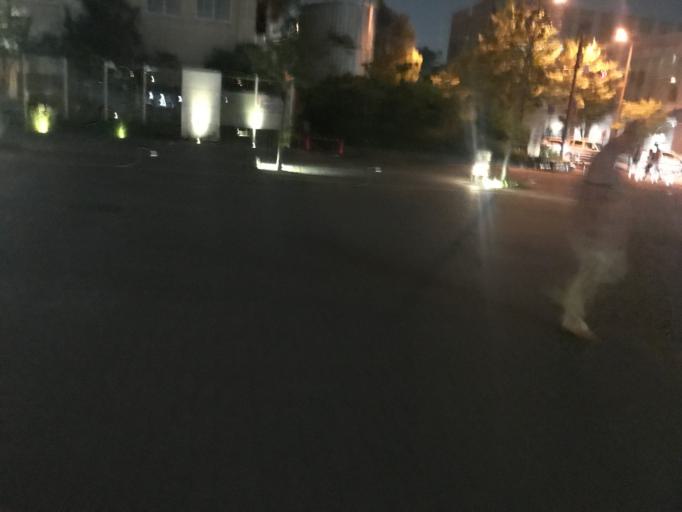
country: JP
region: Aichi
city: Nagoya-shi
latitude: 35.1553
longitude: 136.9670
